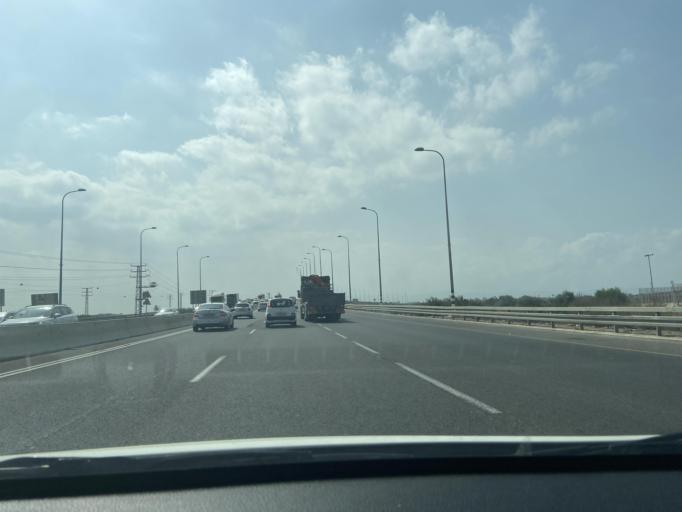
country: IL
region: Northern District
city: `Akko
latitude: 32.9166
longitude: 35.0967
